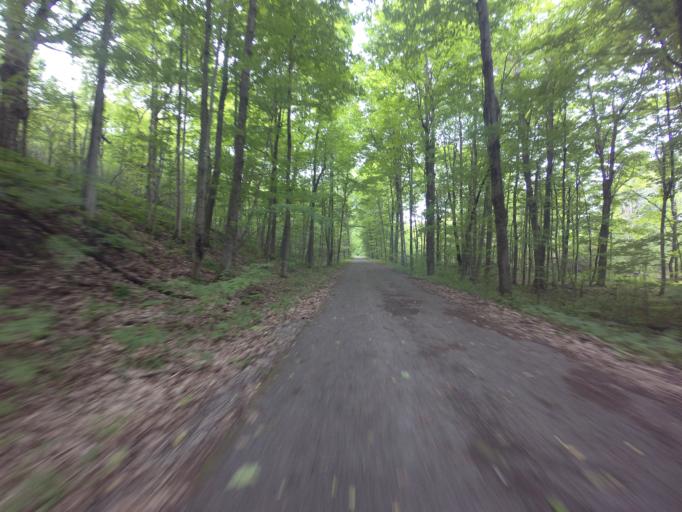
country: US
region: New York
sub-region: Jefferson County
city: Calcium
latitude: 43.9892
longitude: -75.8330
